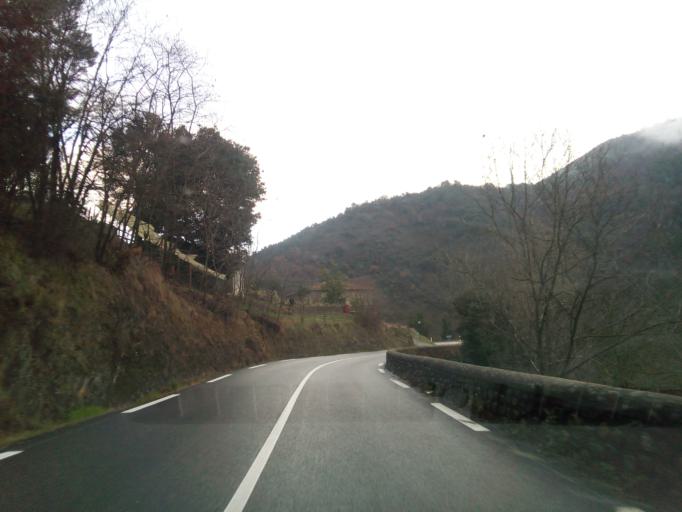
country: FR
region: Rhone-Alpes
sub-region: Departement de l'Ardeche
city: Saint-Sauveur-de-Montagut
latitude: 44.8117
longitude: 4.6372
